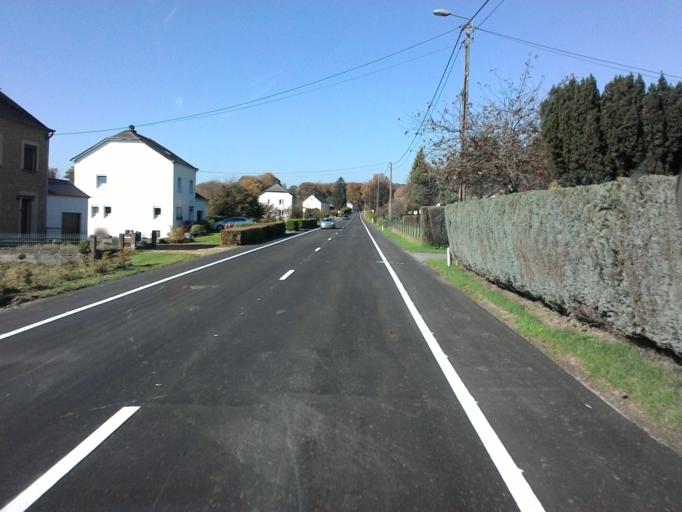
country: BE
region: Wallonia
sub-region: Province du Luxembourg
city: Florenville
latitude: 49.7246
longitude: 5.3141
